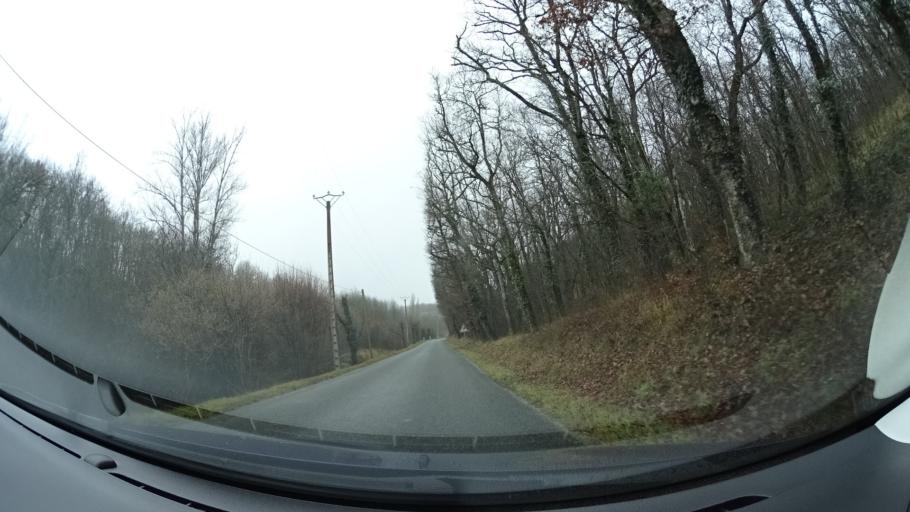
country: FR
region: Midi-Pyrenees
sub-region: Departement du Lot
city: Montcuq
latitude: 44.3887
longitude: 1.2229
